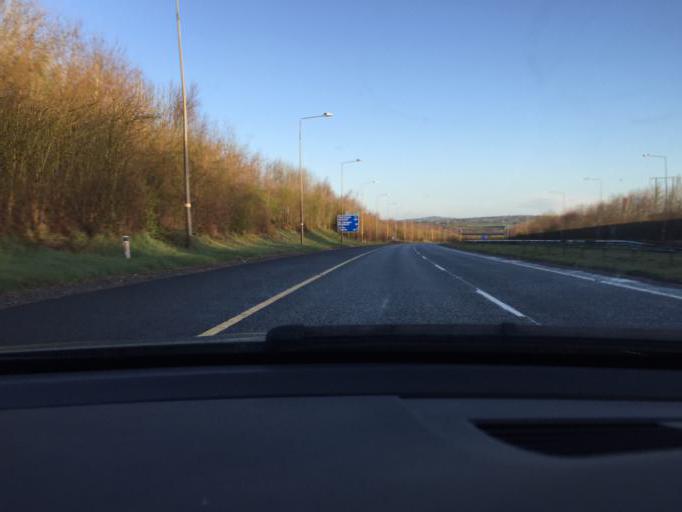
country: IE
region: Leinster
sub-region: Lu
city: Tullyallen
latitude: 53.7073
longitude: -6.3919
